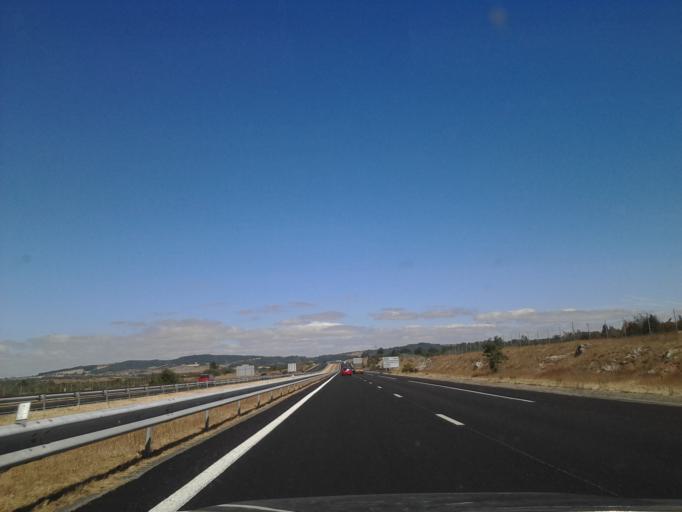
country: FR
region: Midi-Pyrenees
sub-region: Departement de l'Aveyron
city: La Cavalerie
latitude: 43.9387
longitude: 3.2271
